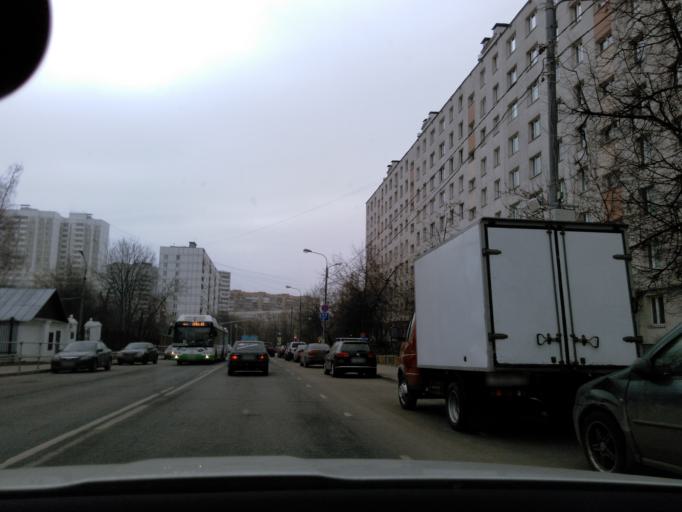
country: RU
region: Moscow
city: Novokhovrino
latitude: 55.8648
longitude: 37.5070
